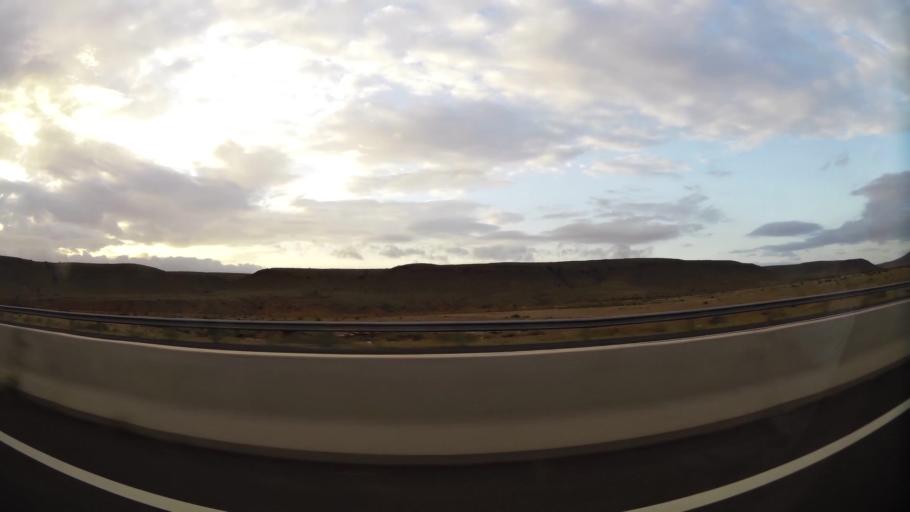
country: MA
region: Oriental
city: Taourirt
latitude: 34.4450
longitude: -3.0637
